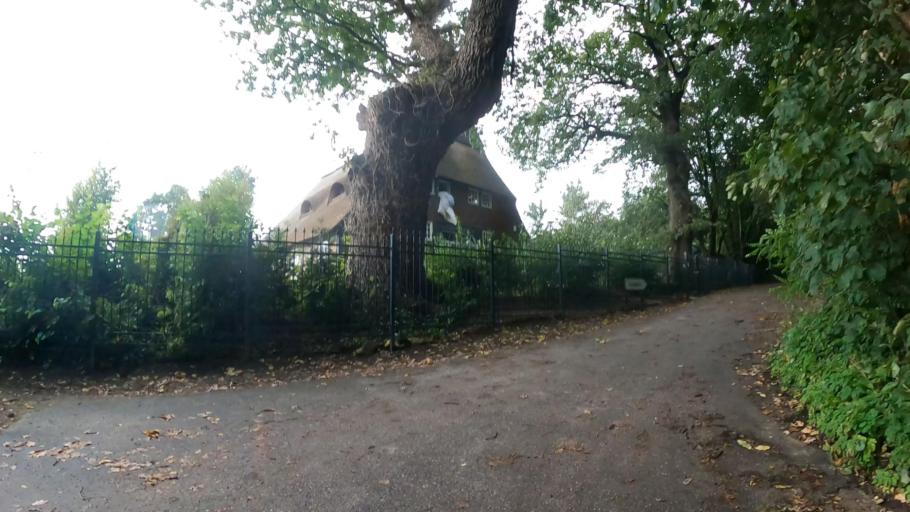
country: DE
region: Schleswig-Holstein
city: Prisdorf
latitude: 53.6685
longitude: 9.7641
